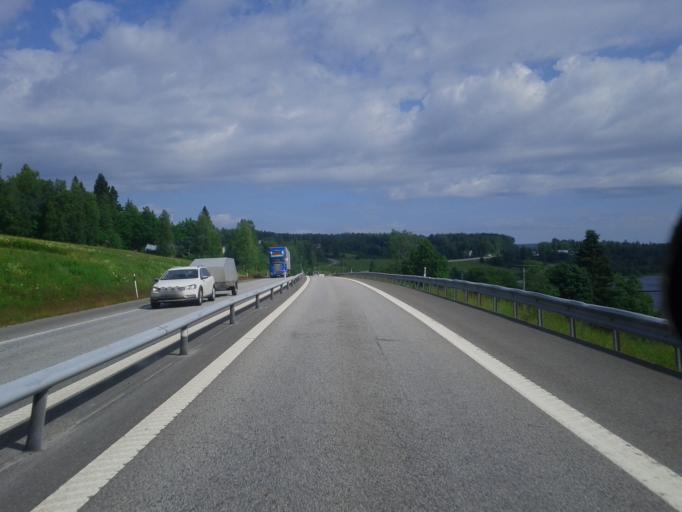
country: SE
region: Vaesternorrland
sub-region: OErnskoeldsviks Kommun
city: Ornskoldsvik
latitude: 63.3023
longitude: 18.9066
